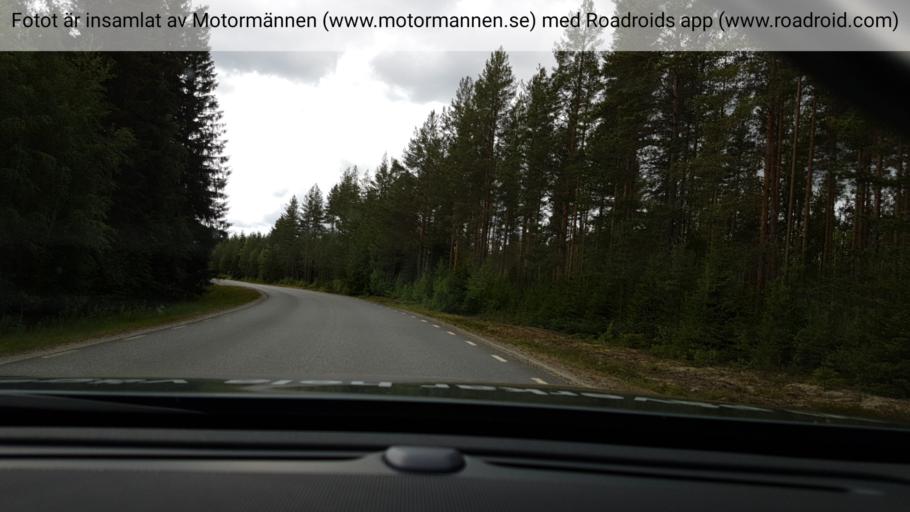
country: SE
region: Vaesterbotten
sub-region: Vindelns Kommun
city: Vindeln
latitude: 64.1842
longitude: 19.6803
